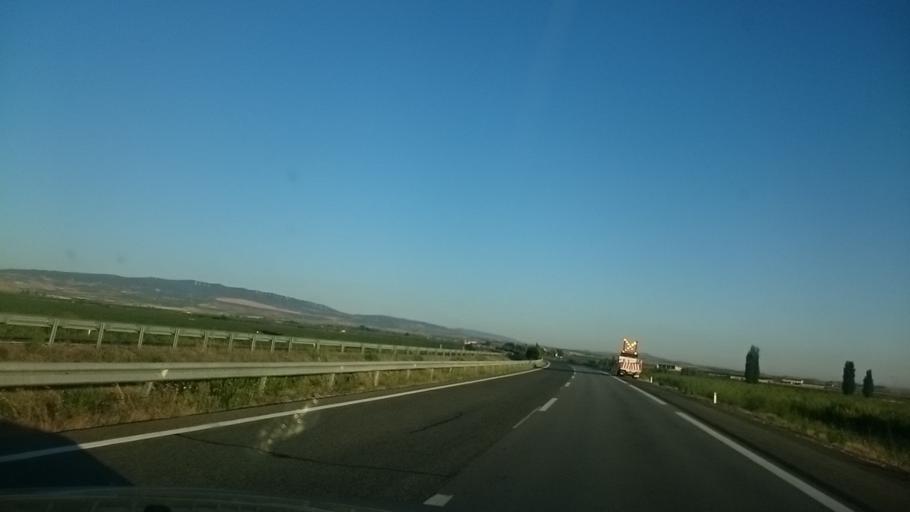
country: ES
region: Navarre
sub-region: Provincia de Navarra
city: Corella
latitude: 42.1489
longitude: -1.7912
